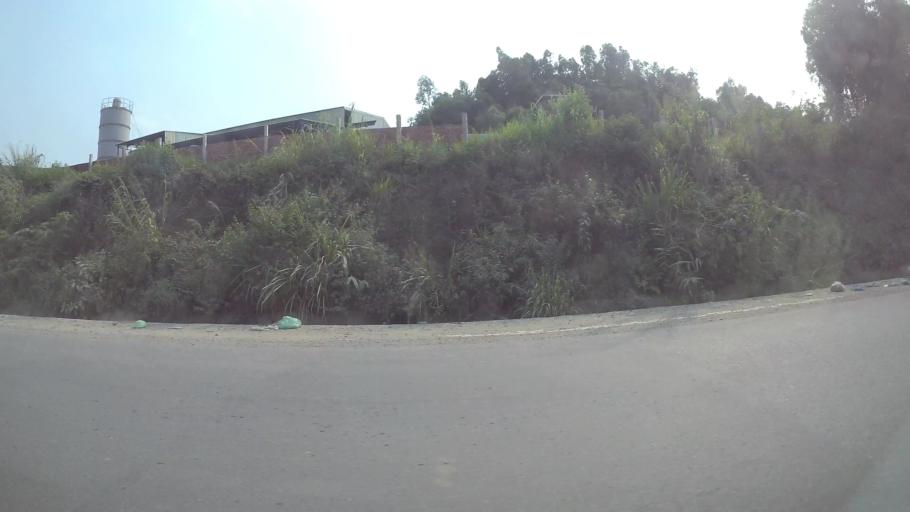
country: VN
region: Da Nang
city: Lien Chieu
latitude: 16.0390
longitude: 108.1717
